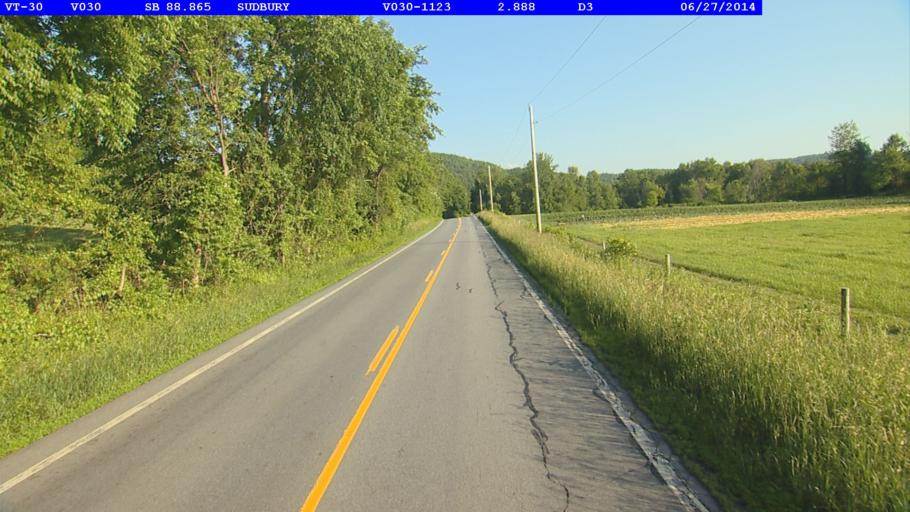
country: US
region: Vermont
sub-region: Rutland County
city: Brandon
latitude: 43.7895
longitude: -73.2040
